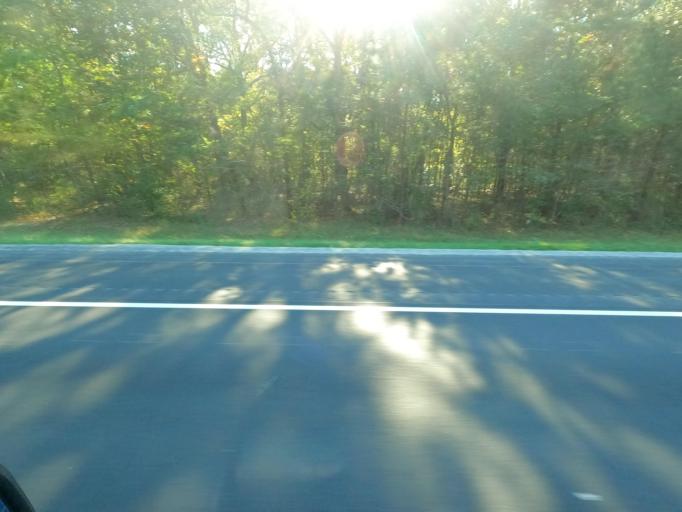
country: US
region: Tennessee
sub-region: Coffee County
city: Manchester
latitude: 35.4208
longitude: -86.0201
